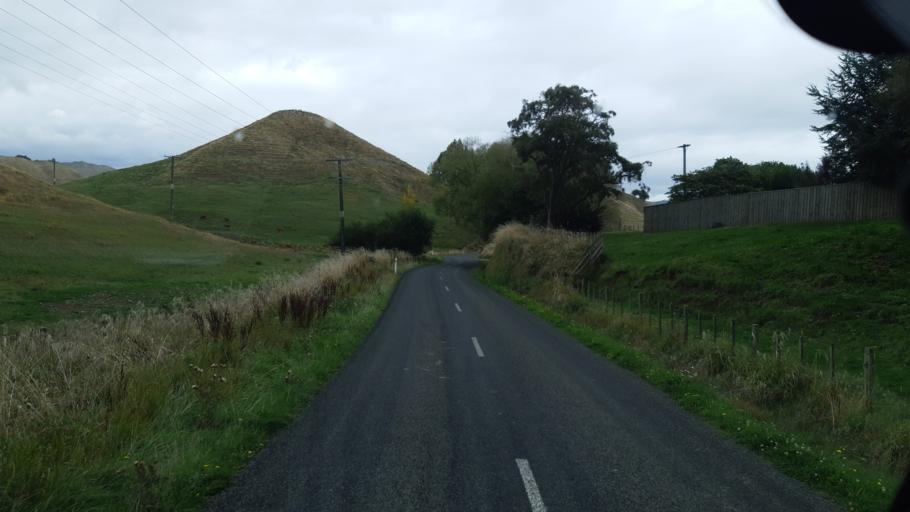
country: NZ
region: Manawatu-Wanganui
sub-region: Ruapehu District
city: Waiouru
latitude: -39.5535
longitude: 175.6020
